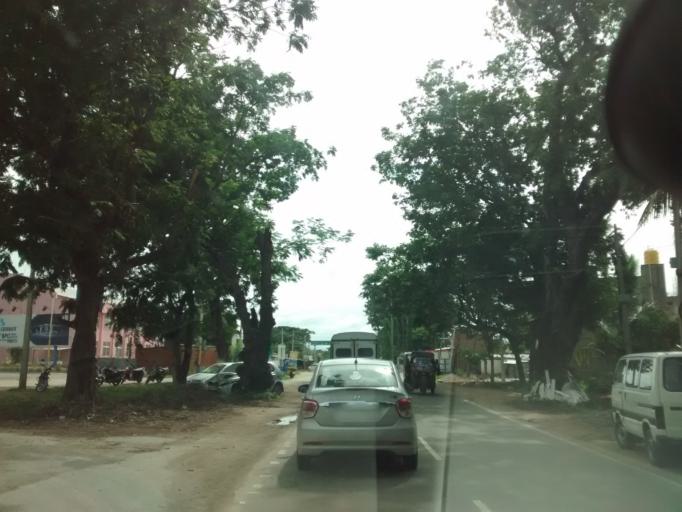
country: IN
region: Karnataka
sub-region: Tumkur
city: Koratagere
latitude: 13.5135
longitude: 77.2267
